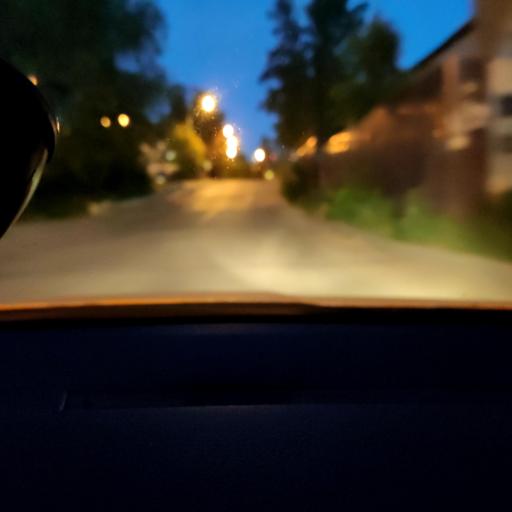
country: RU
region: Moskovskaya
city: Vidnoye
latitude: 55.5555
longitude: 37.6911
